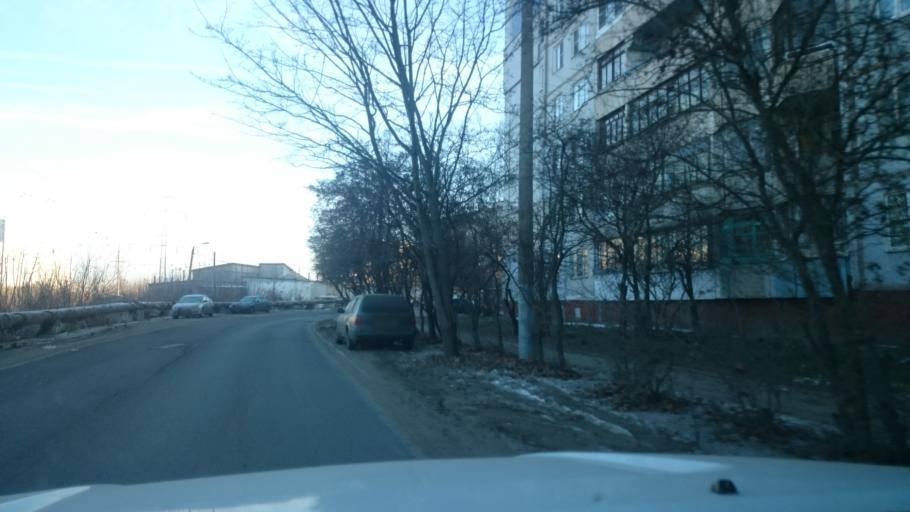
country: RU
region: Tula
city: Tula
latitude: 54.2092
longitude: 37.6832
